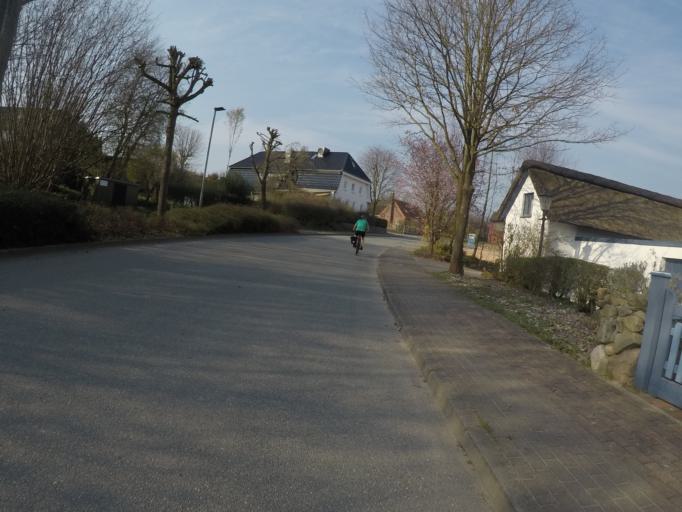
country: DE
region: Schleswig-Holstein
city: Kukels
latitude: 53.8932
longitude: 10.2369
